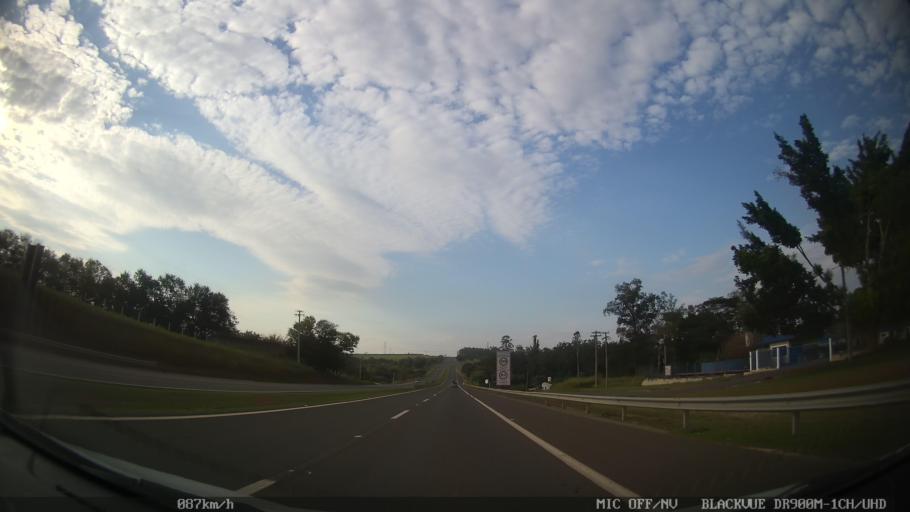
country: BR
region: Sao Paulo
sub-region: Cosmopolis
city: Cosmopolis
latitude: -22.6170
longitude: -47.1979
